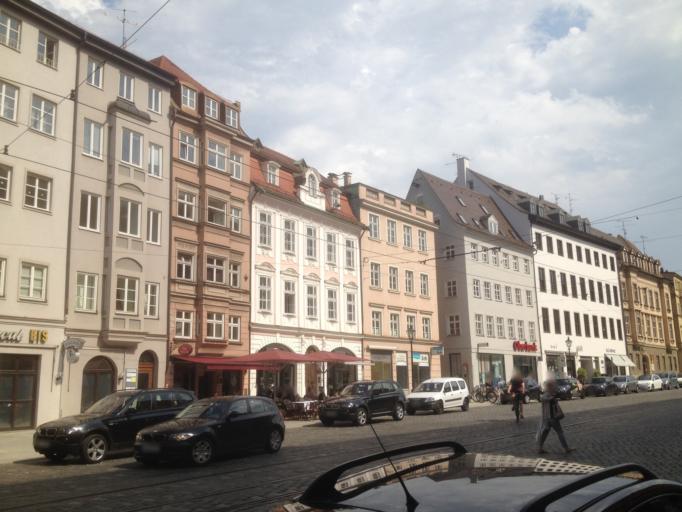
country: DE
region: Bavaria
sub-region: Swabia
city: Augsburg
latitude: 48.3664
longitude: 10.8989
